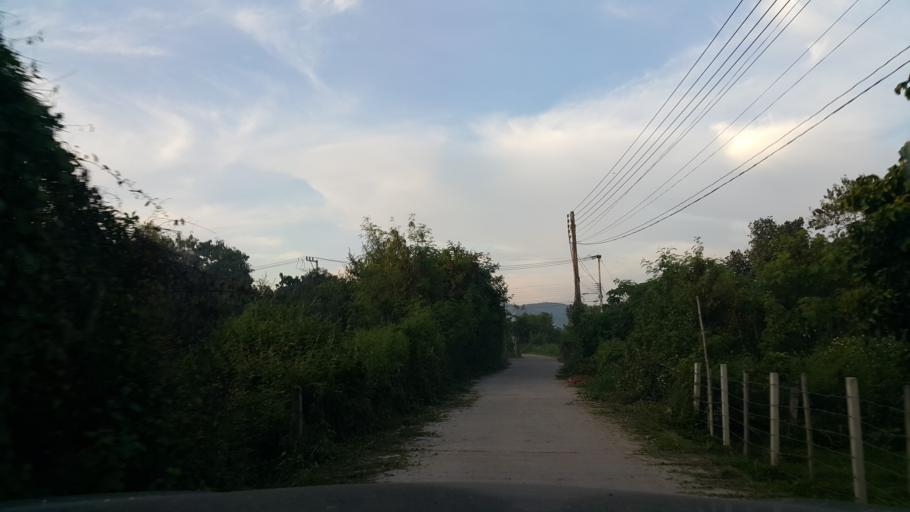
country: TH
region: Chiang Mai
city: San Sai
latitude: 18.8956
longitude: 99.0866
